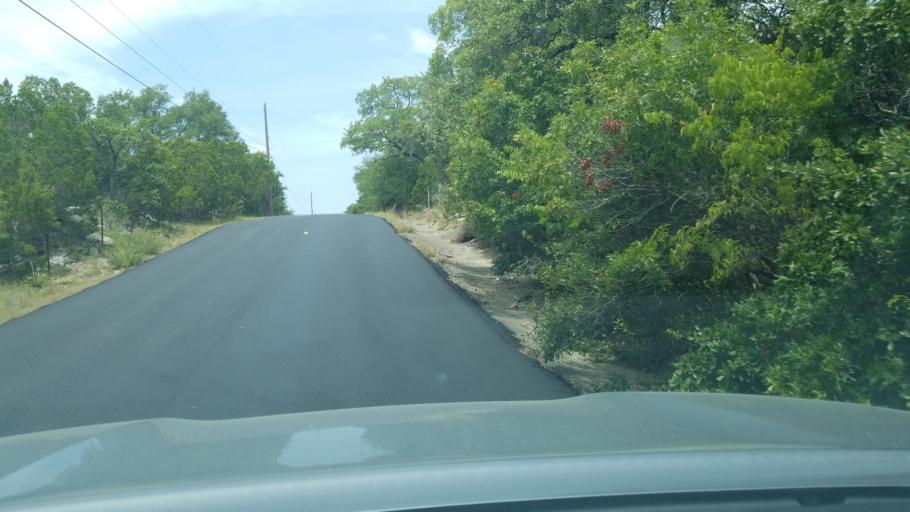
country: US
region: Texas
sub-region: Comal County
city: Bulverde
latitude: 29.7598
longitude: -98.4688
